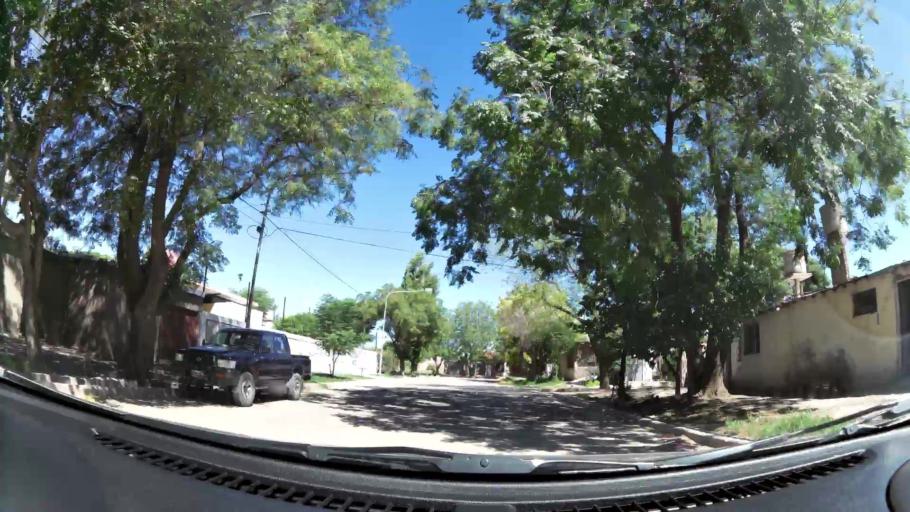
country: AR
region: Mendoza
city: Las Heras
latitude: -32.8326
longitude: -68.8360
